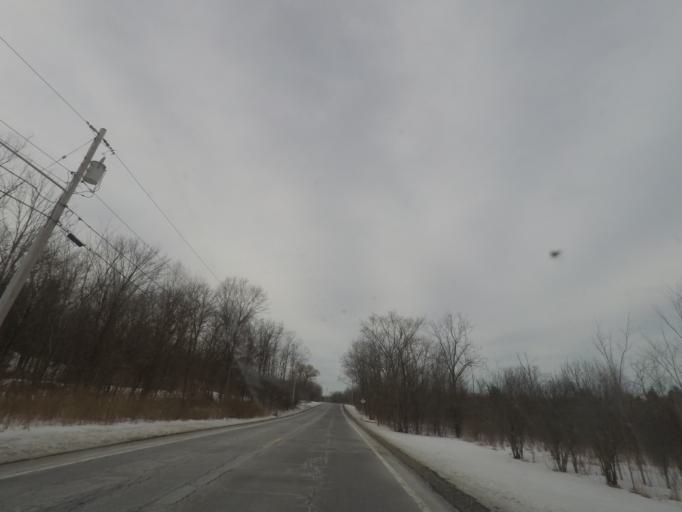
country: US
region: New York
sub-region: Albany County
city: Altamont
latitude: 42.6870
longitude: -74.0224
